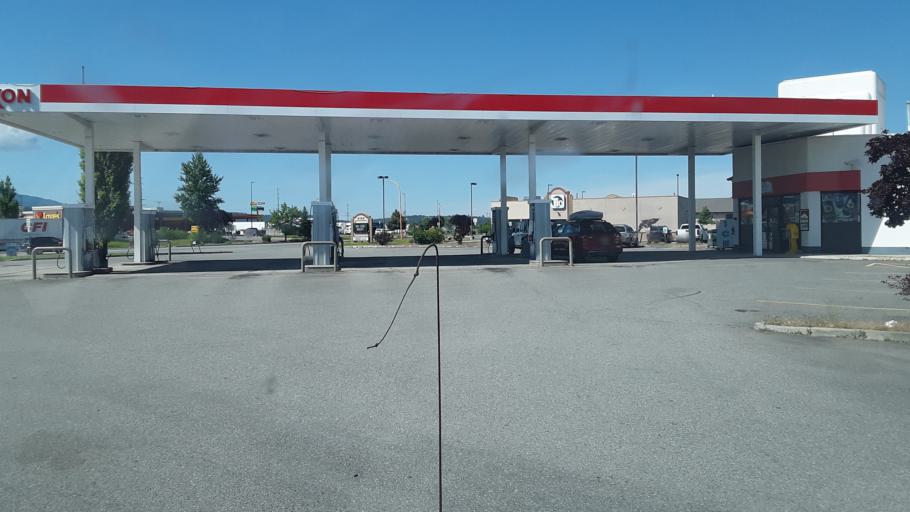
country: US
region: Idaho
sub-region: Kootenai County
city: Post Falls
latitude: 47.7127
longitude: -117.0021
